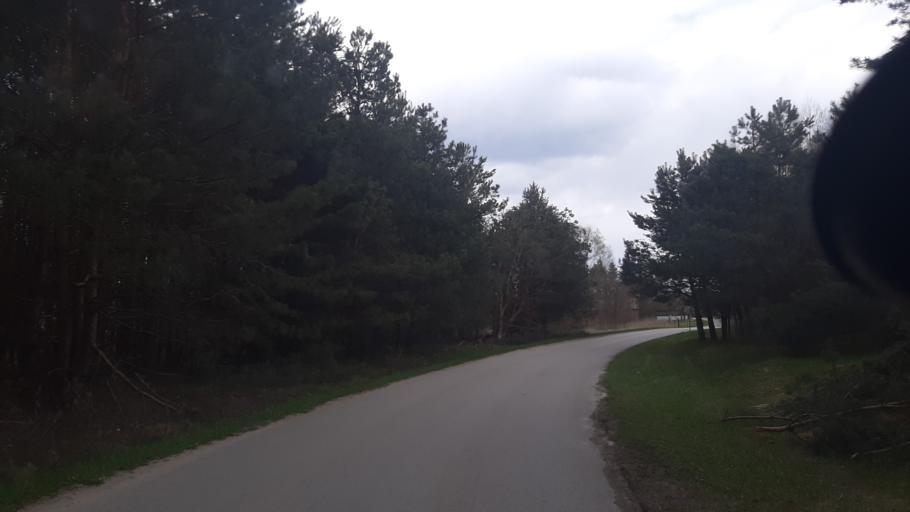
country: PL
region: Lublin Voivodeship
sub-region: Powiat lubelski
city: Niemce
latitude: 51.3807
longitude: 22.5550
